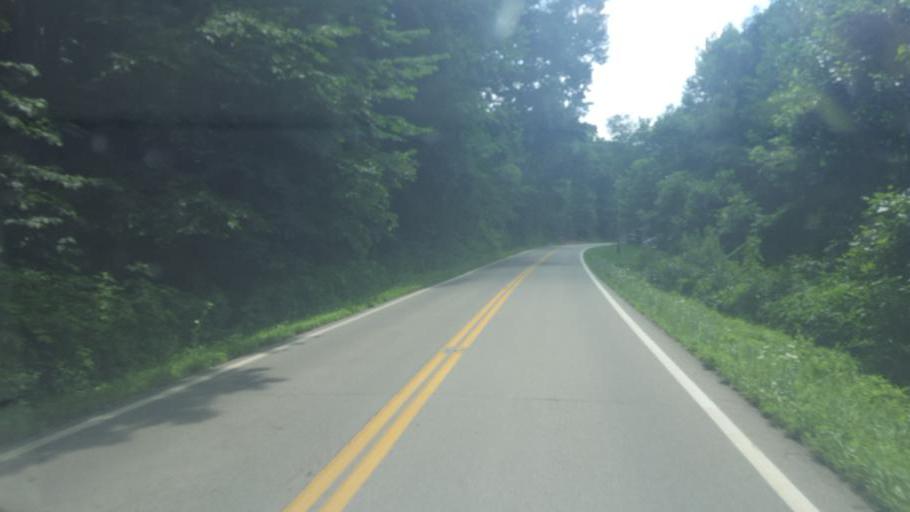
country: US
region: Ohio
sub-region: Ross County
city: Kingston
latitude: 39.4021
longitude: -82.7362
